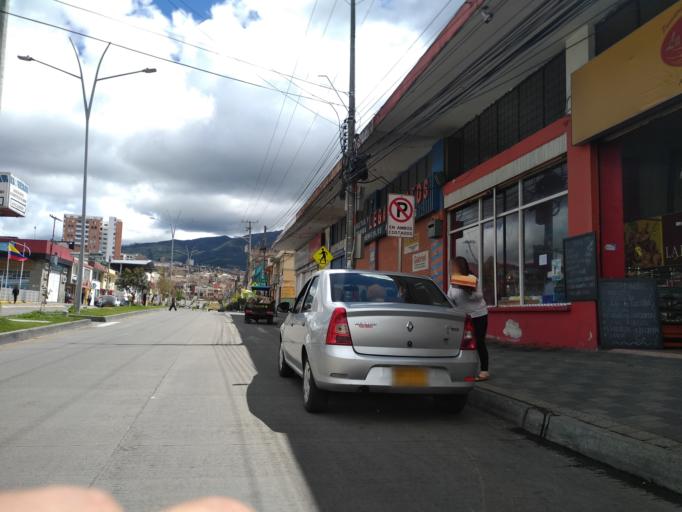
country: CO
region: Narino
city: Pasto
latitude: 1.2079
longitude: -77.2779
